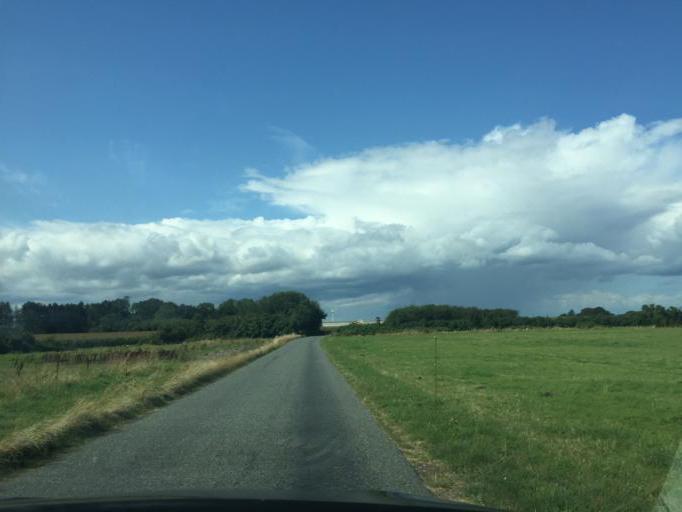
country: DK
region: South Denmark
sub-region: Faaborg-Midtfyn Kommune
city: Arslev
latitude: 55.3236
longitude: 10.4889
